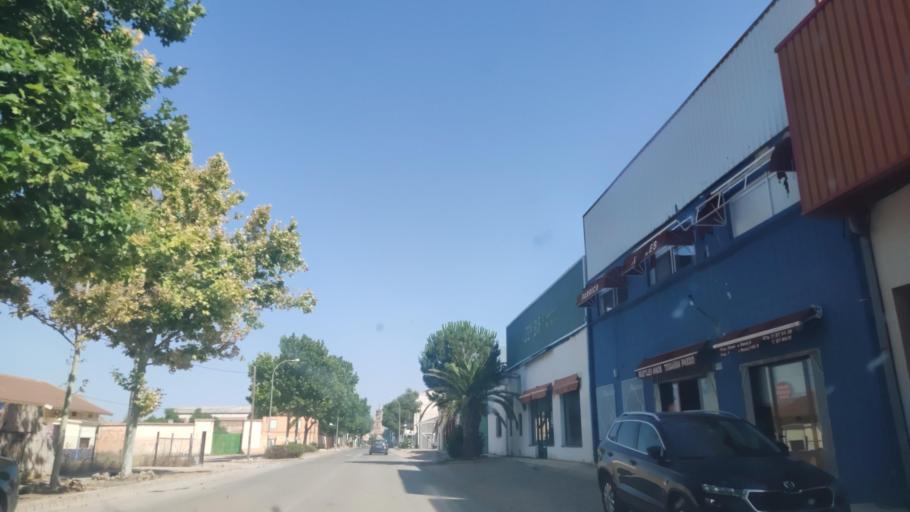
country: ES
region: Castille-La Mancha
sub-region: Provincia de Albacete
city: La Gineta
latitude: 39.1095
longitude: -1.9924
